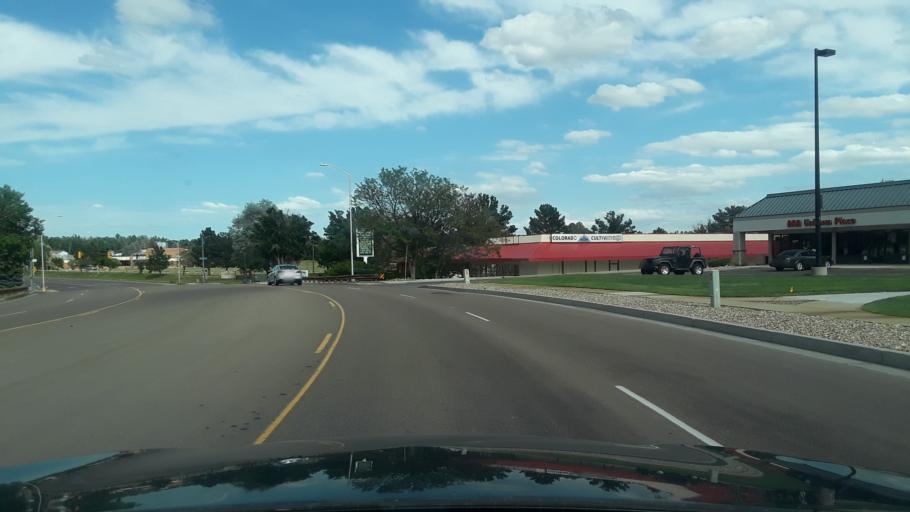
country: US
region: Colorado
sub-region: El Paso County
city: Cimarron Hills
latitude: 38.8821
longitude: -104.7553
